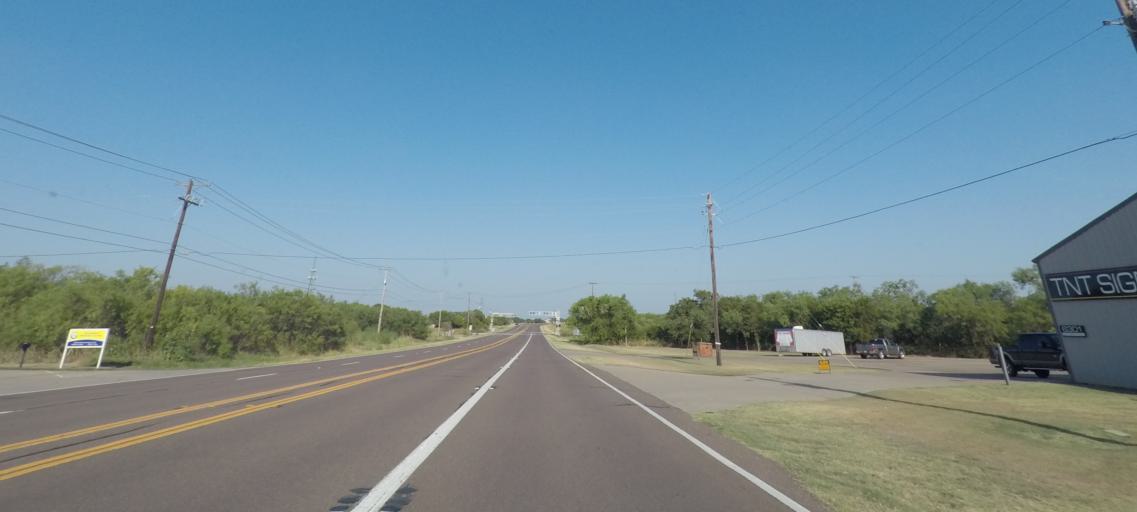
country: US
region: Texas
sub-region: Archer County
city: Holliday
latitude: 33.8593
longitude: -98.5945
